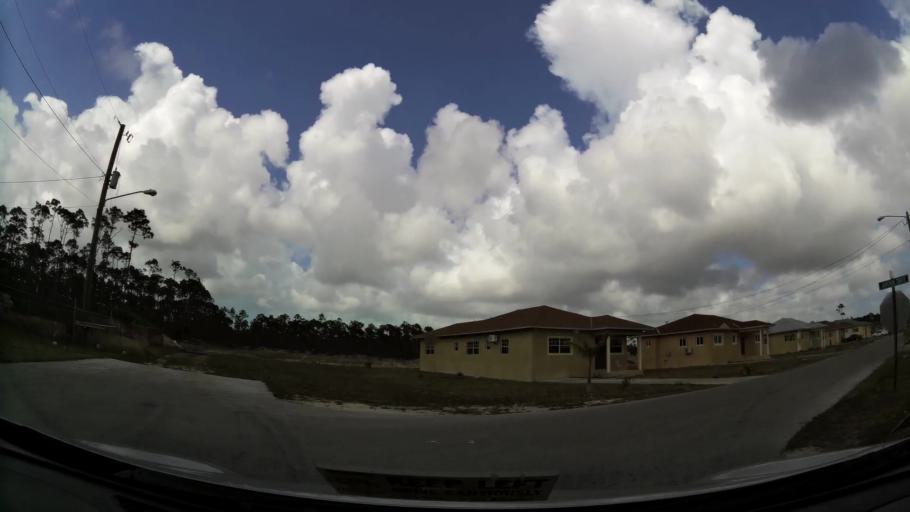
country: BS
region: Freeport
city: Freeport
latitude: 26.5199
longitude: -78.7275
